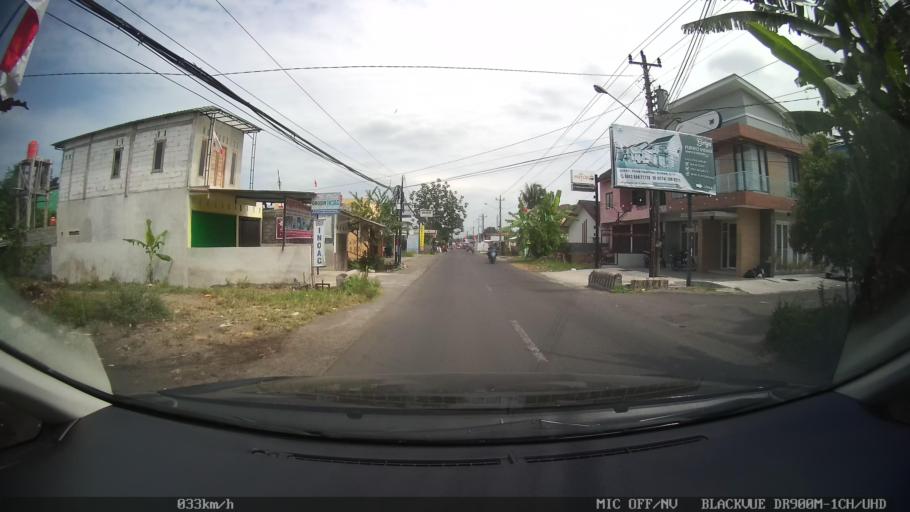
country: ID
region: Daerah Istimewa Yogyakarta
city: Depok
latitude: -7.7409
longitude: 110.4517
